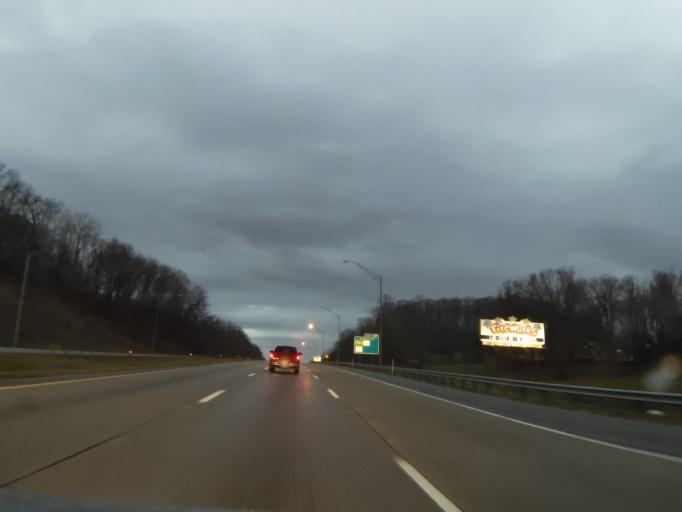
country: US
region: Tennessee
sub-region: Washington County
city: Oak Grove
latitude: 36.3593
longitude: -82.4032
